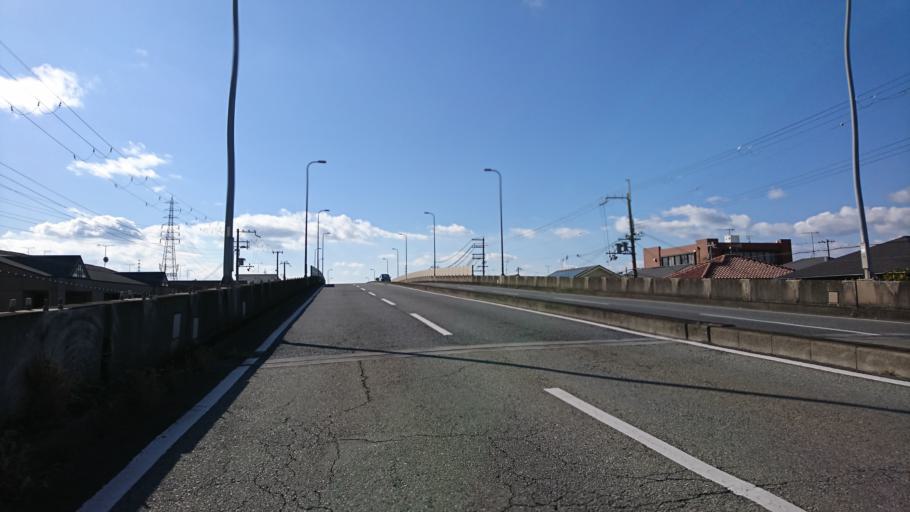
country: JP
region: Hyogo
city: Kakogawacho-honmachi
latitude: 34.7508
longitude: 134.8198
